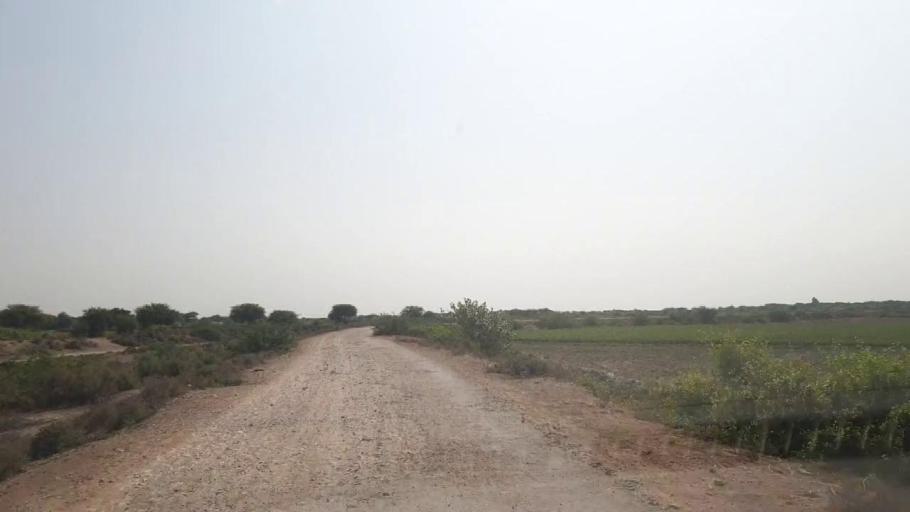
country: PK
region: Sindh
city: Kadhan
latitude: 24.4656
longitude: 68.9057
